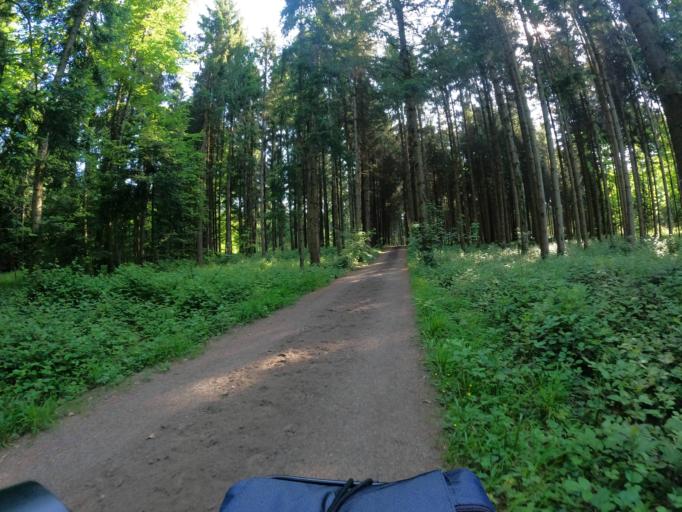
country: CH
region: Zug
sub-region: Zug
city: Steinhausen
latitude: 47.2124
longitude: 8.4995
